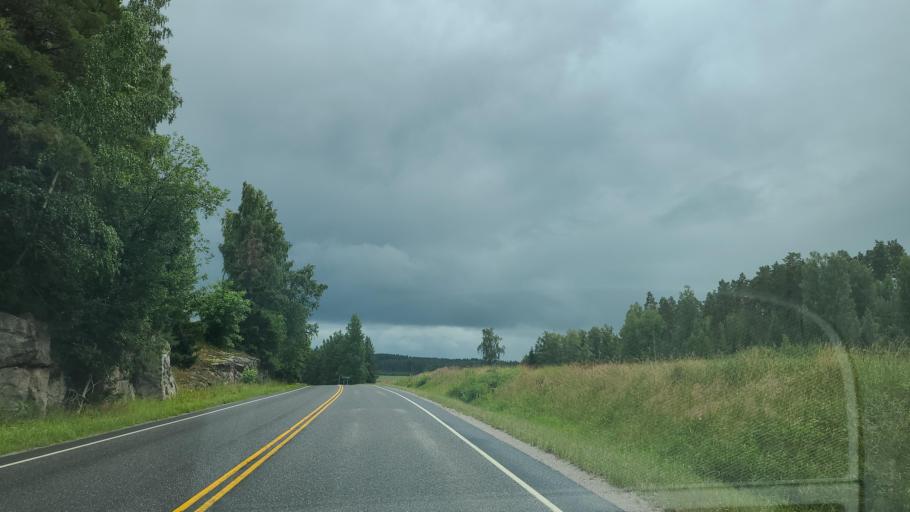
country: FI
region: Varsinais-Suomi
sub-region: Turku
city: Sauvo
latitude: 60.3368
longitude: 22.7029
